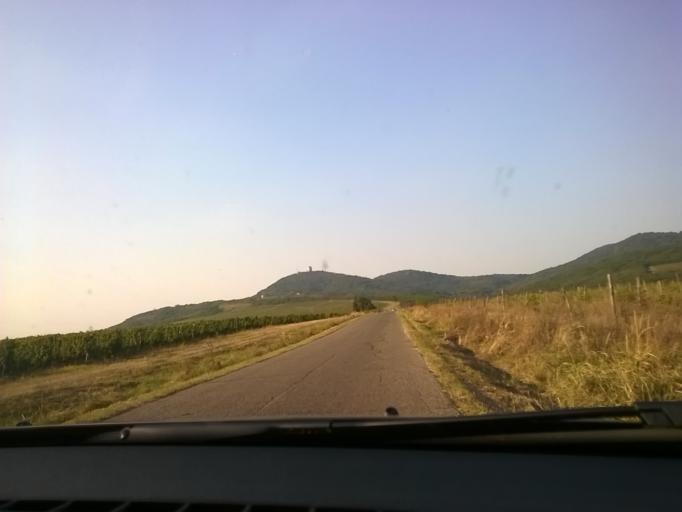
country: RS
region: Autonomna Pokrajina Vojvodina
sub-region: Juznobanatski Okrug
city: Vrsac
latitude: 45.1011
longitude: 21.3280
